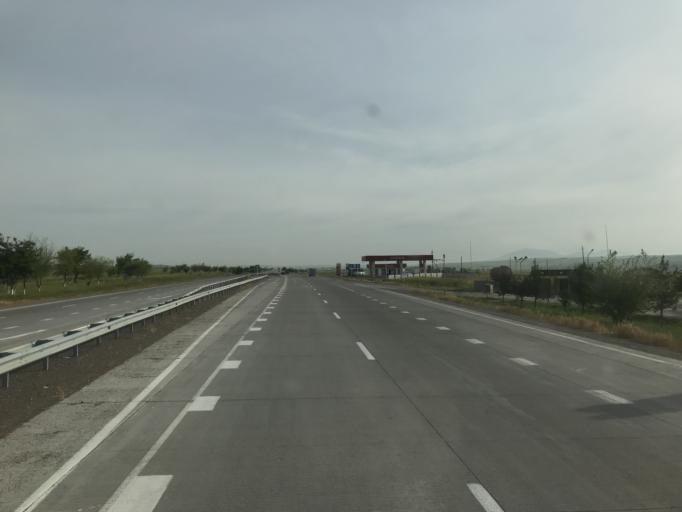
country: KZ
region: Ongtustik Qazaqstan
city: Qazyqurt
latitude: 41.8083
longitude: 69.3964
